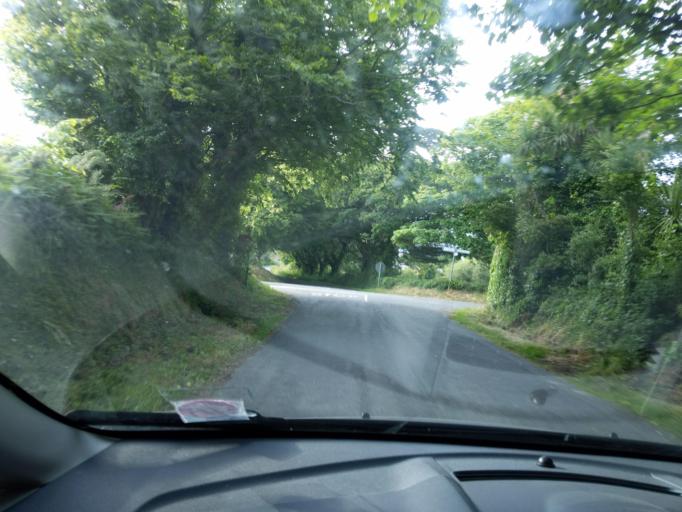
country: IM
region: Ramsey
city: Ramsey
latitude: 54.3479
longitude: -4.4488
